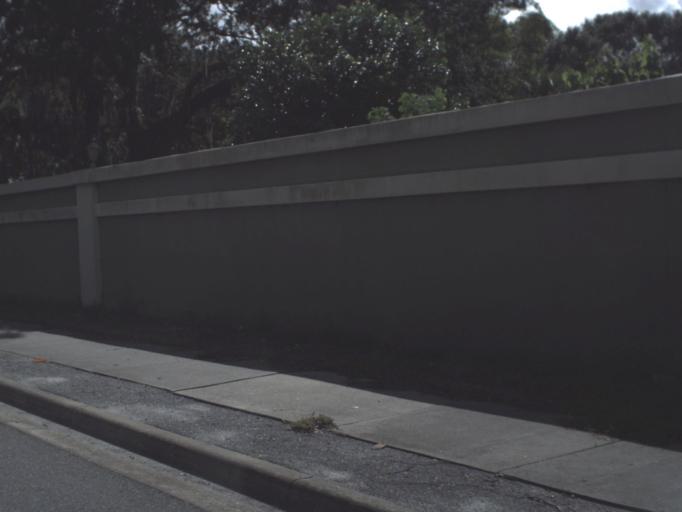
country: US
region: Florida
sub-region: Sarasota County
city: Sarasota
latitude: 27.3374
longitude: -82.5188
